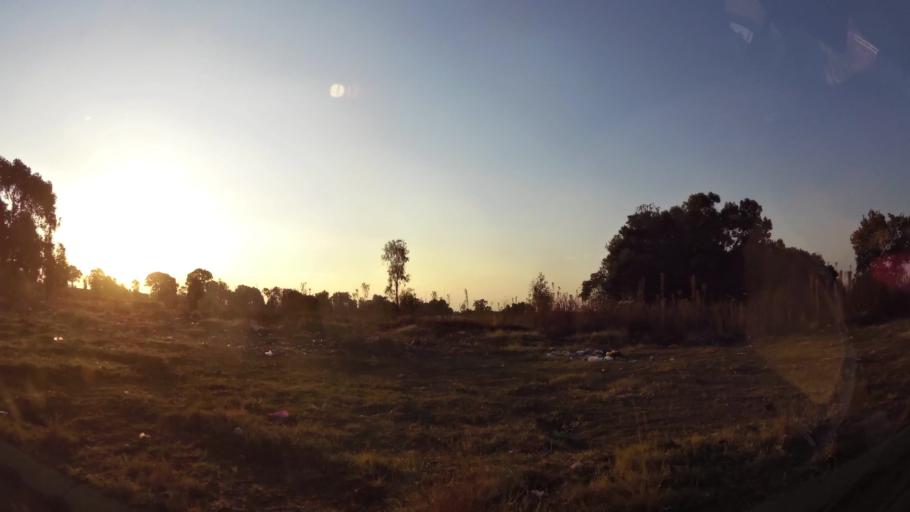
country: ZA
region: Gauteng
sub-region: West Rand District Municipality
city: Randfontein
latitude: -26.2084
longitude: 27.7018
